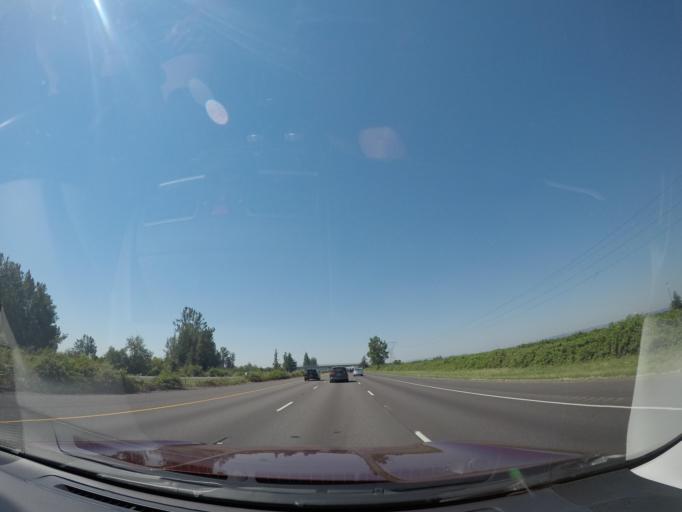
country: US
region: Oregon
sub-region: Marion County
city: Gervais
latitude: 45.0915
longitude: -122.9415
